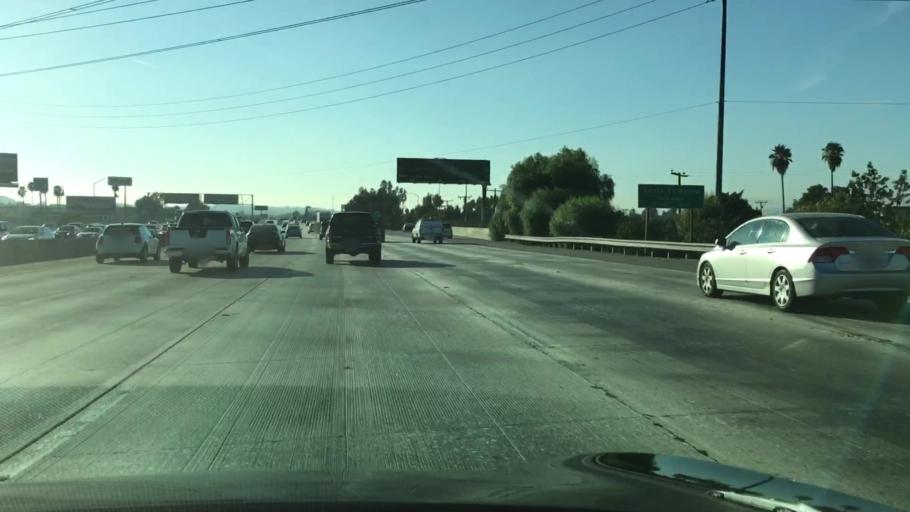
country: US
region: California
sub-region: Los Angeles County
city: South El Monte
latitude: 34.0371
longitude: -118.0341
